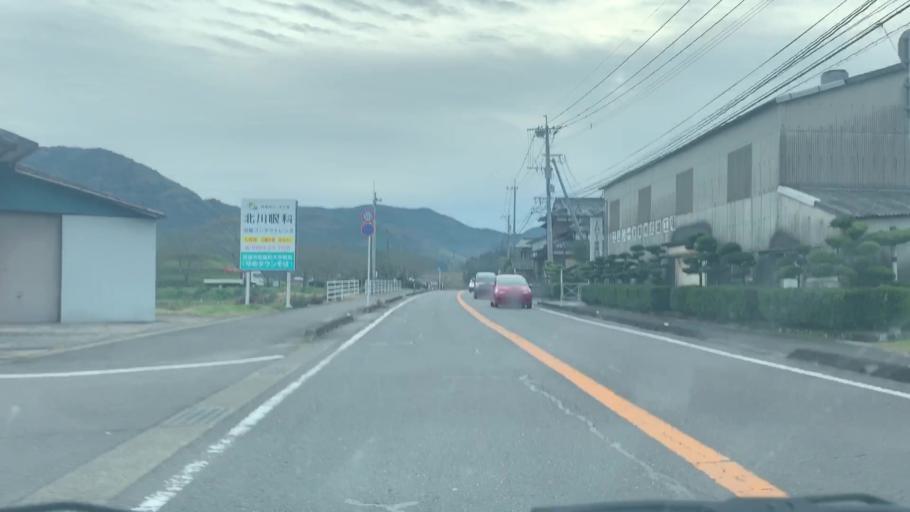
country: JP
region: Saga Prefecture
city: Takeocho-takeo
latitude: 33.1676
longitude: 130.0533
